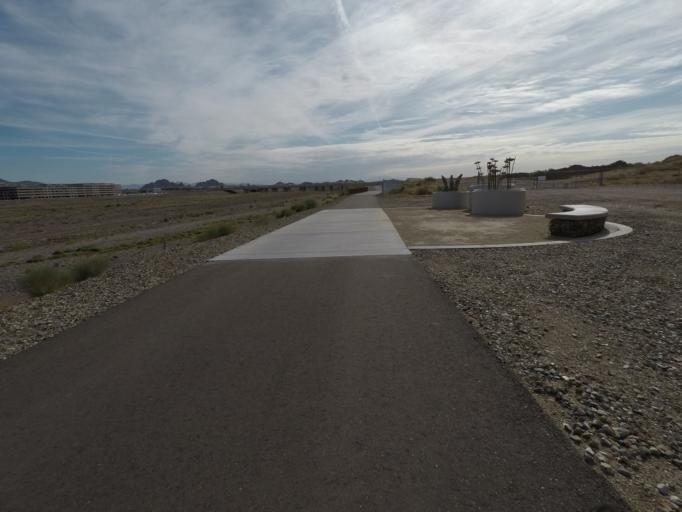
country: US
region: Arizona
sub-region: Maricopa County
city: Tempe Junction
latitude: 33.4286
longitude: -111.9855
